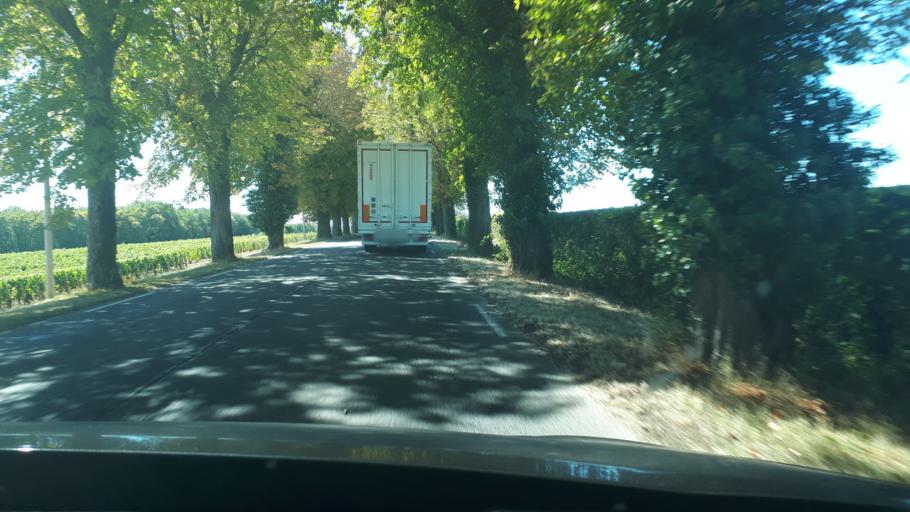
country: FR
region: Centre
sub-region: Departement du Cher
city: Sancerre
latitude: 47.3169
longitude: 2.8142
